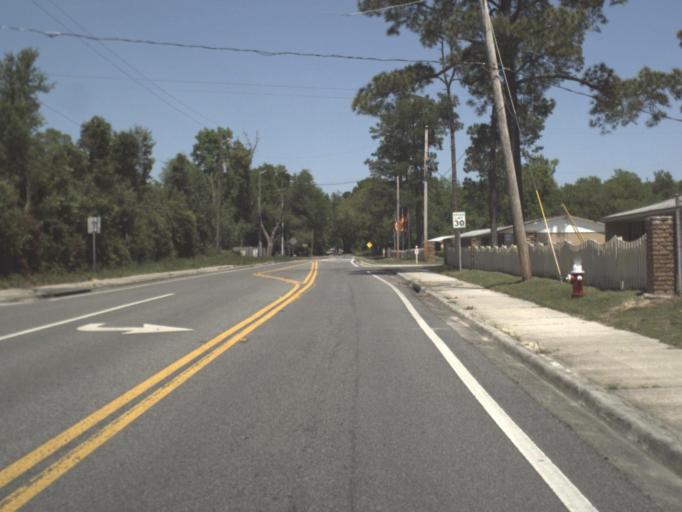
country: US
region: Florida
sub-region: Escambia County
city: Ferry Pass
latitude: 30.4960
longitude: -87.2327
